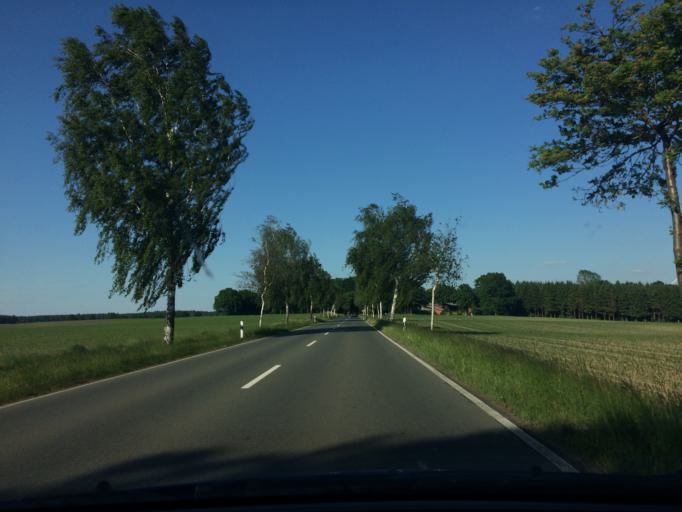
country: DE
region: Lower Saxony
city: Soltau
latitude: 53.0295
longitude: 9.9179
